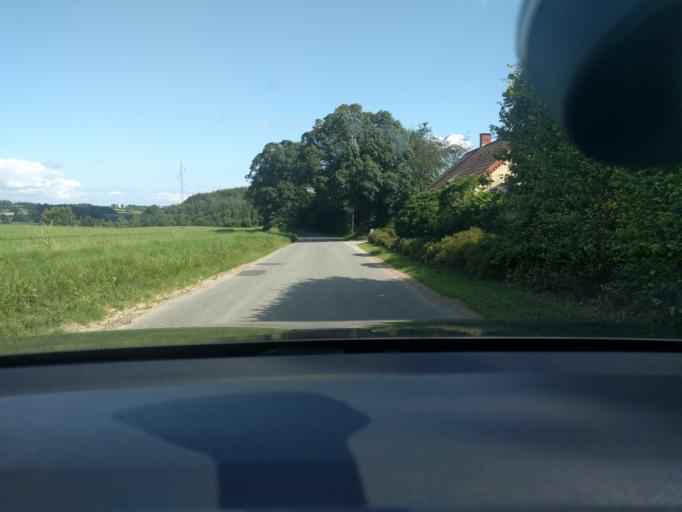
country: DK
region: Central Jutland
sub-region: Viborg Kommune
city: Viborg
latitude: 56.5063
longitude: 9.3049
